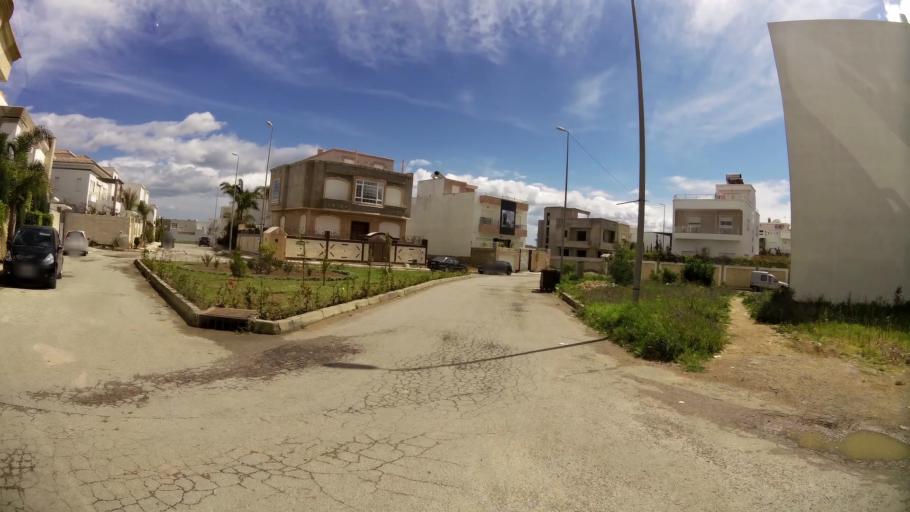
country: MA
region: Tanger-Tetouan
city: Tetouan
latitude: 35.5842
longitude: -5.3352
